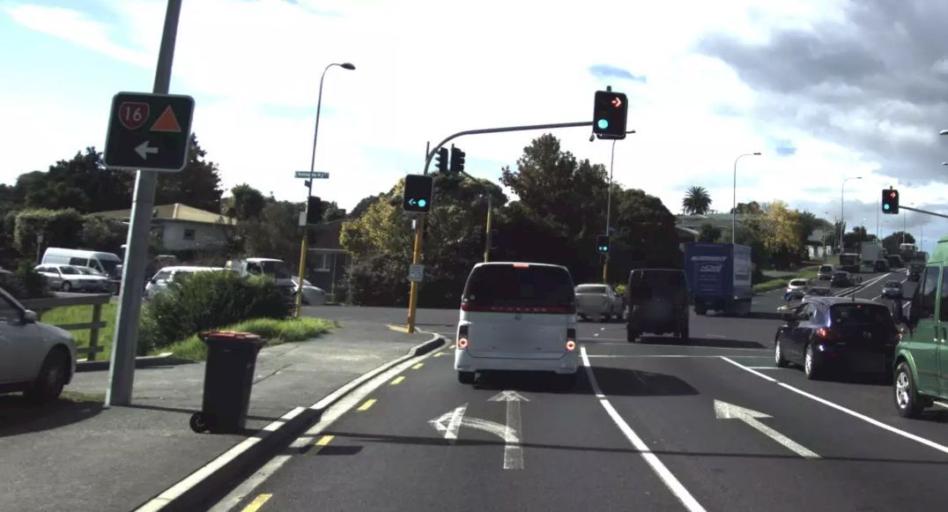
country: NZ
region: Auckland
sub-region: Auckland
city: Rosebank
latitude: -36.9061
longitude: 174.7012
